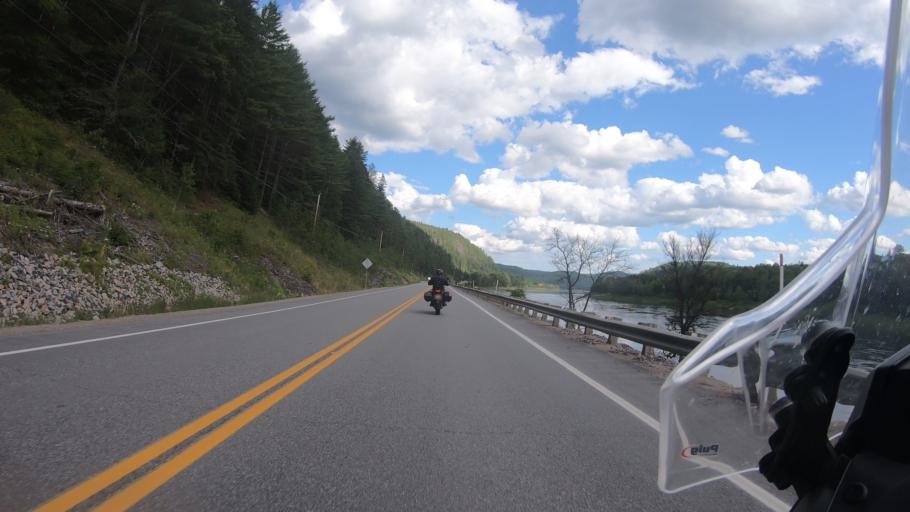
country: CA
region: Quebec
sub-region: Mauricie
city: Saint-Tite
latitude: 46.9979
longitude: -72.9224
